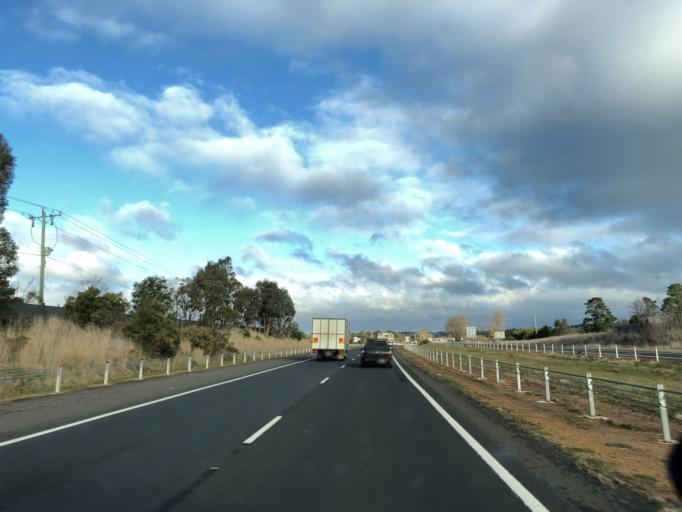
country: AU
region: Victoria
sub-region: Mount Alexander
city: Castlemaine
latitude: -37.2091
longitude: 144.4118
